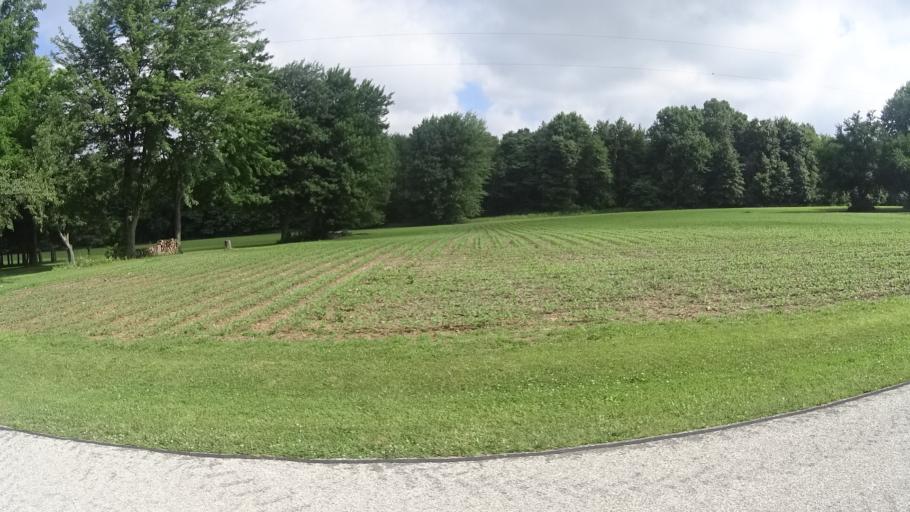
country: US
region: Ohio
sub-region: Huron County
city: Wakeman
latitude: 41.2955
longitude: -82.4458
